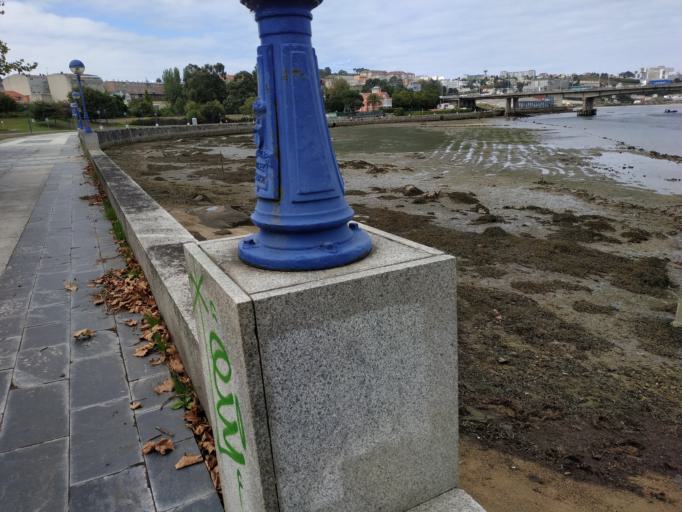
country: ES
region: Galicia
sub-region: Provincia da Coruna
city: Culleredo
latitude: 43.3294
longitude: -8.3801
